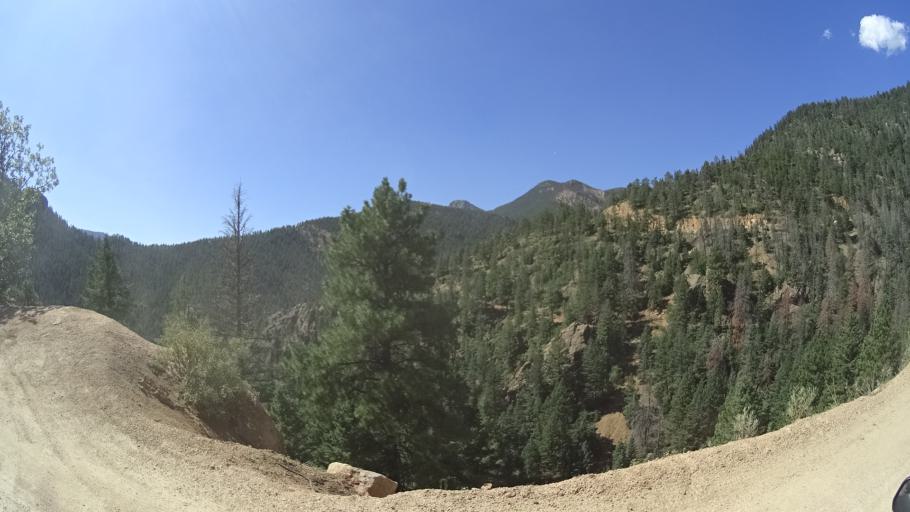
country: US
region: Colorado
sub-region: El Paso County
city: Manitou Springs
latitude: 38.7930
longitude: -104.8949
